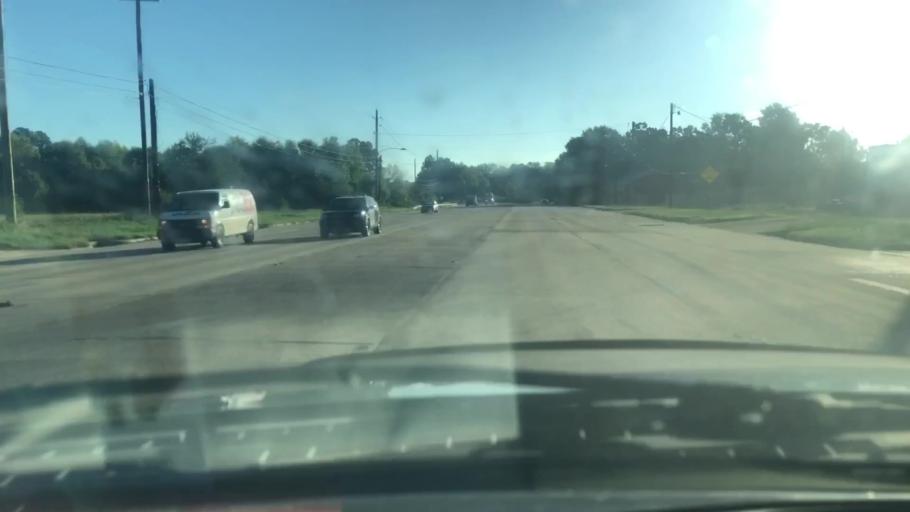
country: US
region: Texas
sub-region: Bowie County
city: Texarkana
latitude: 33.4216
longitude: -94.0752
